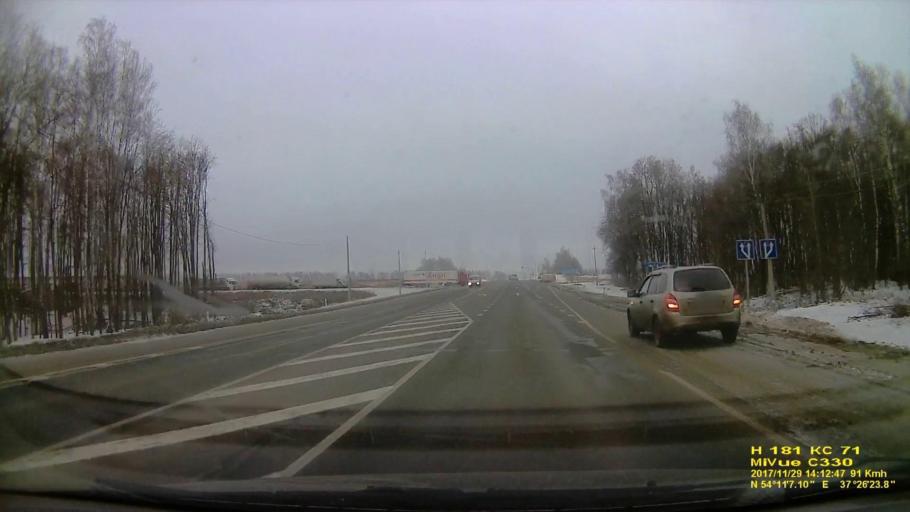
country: RU
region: Tula
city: Barsuki
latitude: 54.1852
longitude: 37.4402
